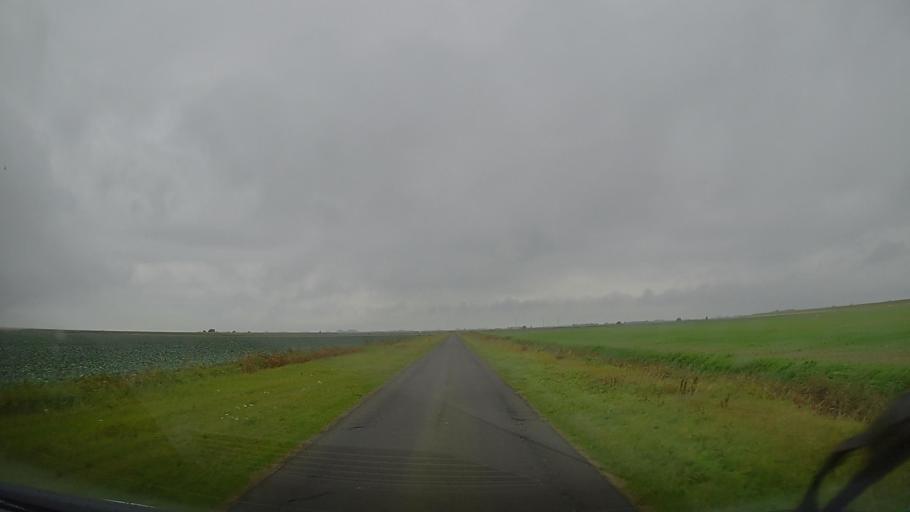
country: DE
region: Schleswig-Holstein
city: Friedrichsgabekoog
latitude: 54.1100
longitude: 8.9836
